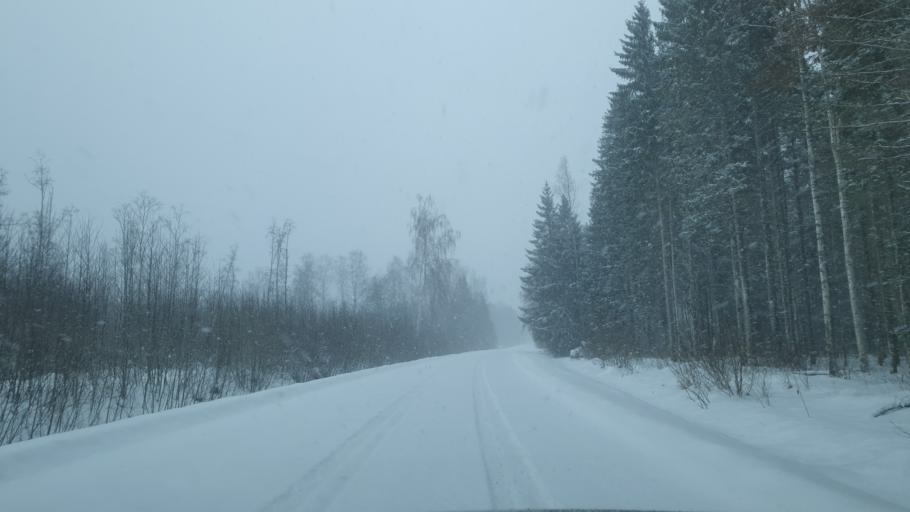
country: EE
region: Jogevamaa
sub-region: Jogeva linn
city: Jogeva
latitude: 58.8061
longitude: 26.4168
